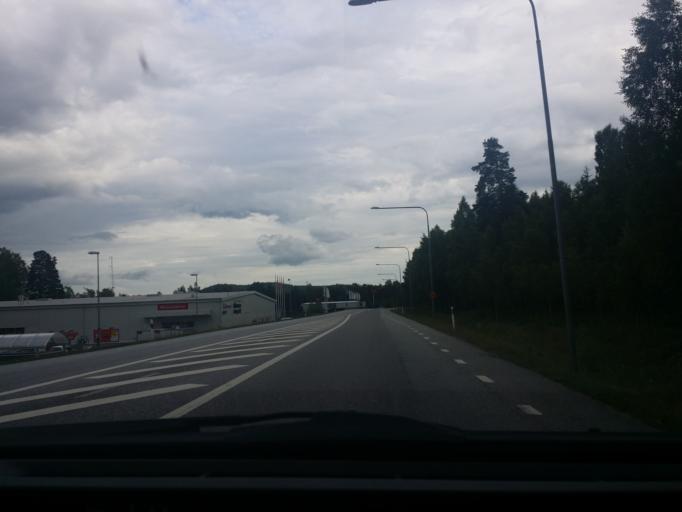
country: SE
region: OErebro
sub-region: Nora Kommun
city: Nora
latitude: 59.5131
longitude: 15.0223
